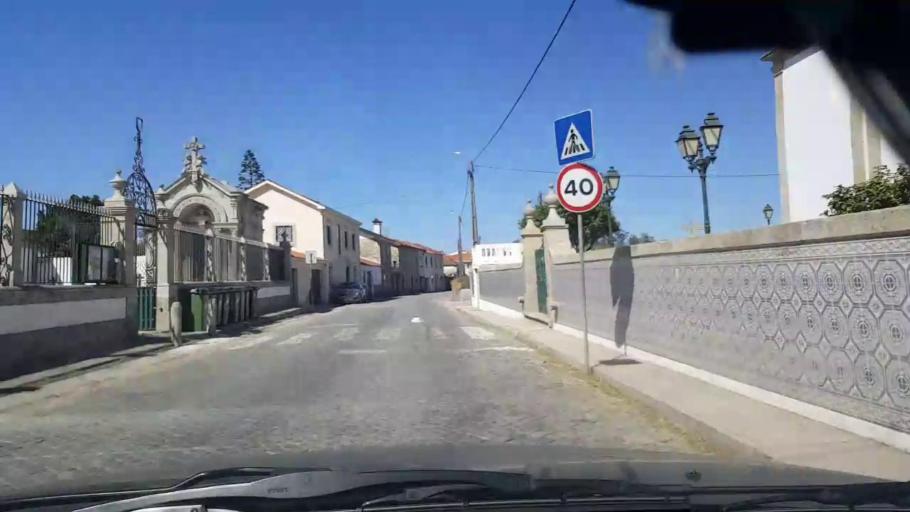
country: PT
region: Porto
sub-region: Vila do Conde
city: Arvore
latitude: 41.3245
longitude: -8.7045
